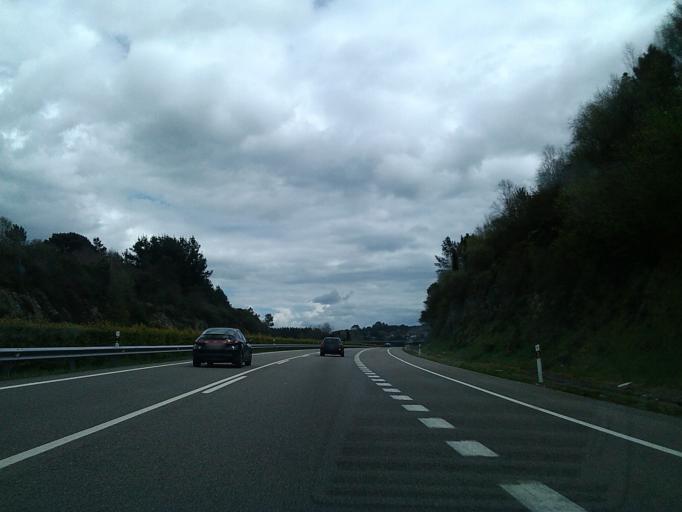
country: ES
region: Galicia
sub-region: Provincia de Lugo
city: Guitiriz
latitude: 43.1905
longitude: -7.9008
